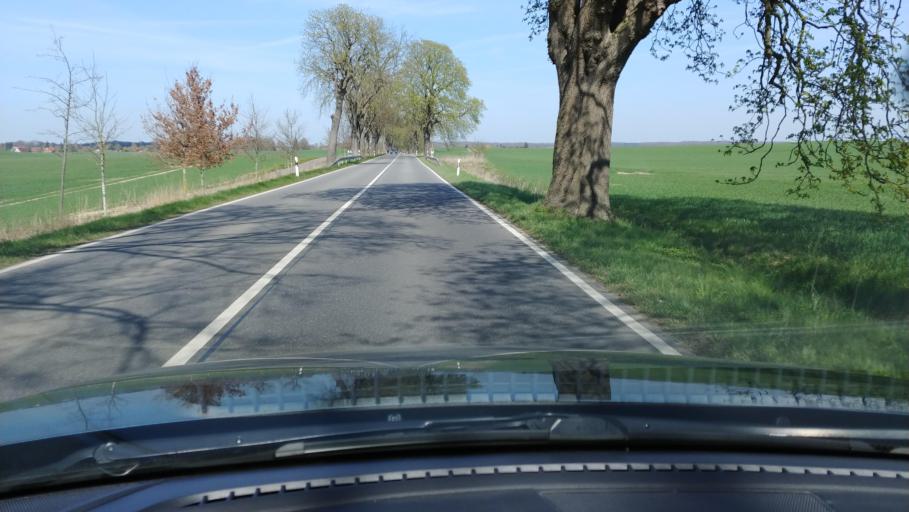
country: DE
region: Mecklenburg-Vorpommern
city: Lubstorf
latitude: 53.7457
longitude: 11.4098
